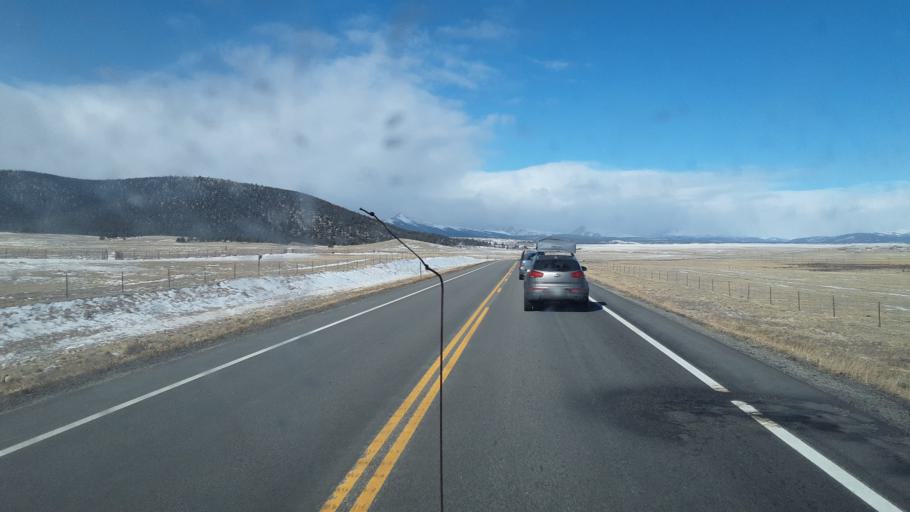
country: US
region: Colorado
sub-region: Park County
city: Fairplay
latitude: 39.0899
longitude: -105.9829
